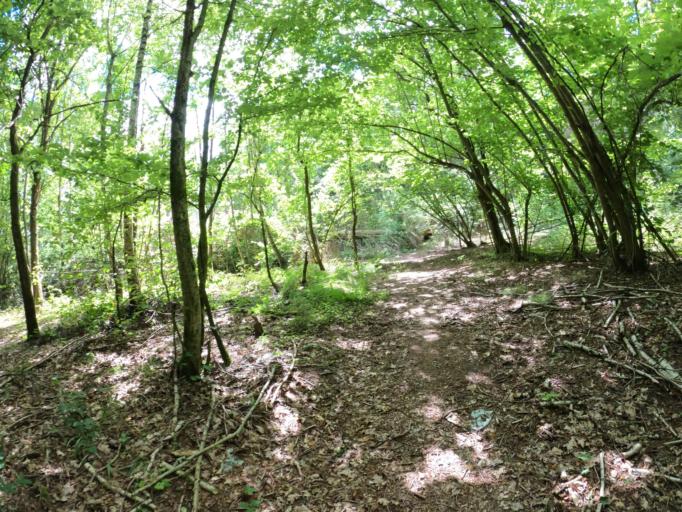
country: PL
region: West Pomeranian Voivodeship
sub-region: Powiat swidwinski
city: Swidwin
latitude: 53.7552
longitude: 15.8176
